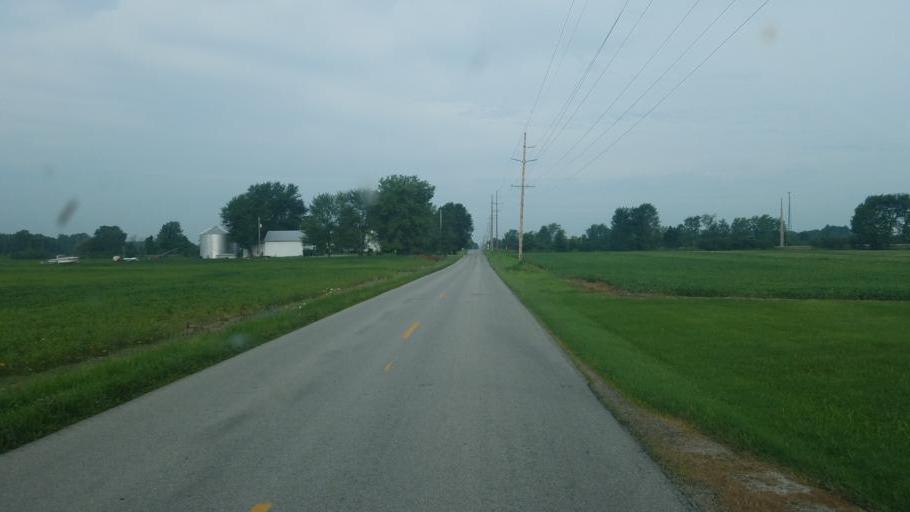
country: US
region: Ohio
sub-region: Morrow County
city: Cardington
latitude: 40.4679
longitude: -82.9134
